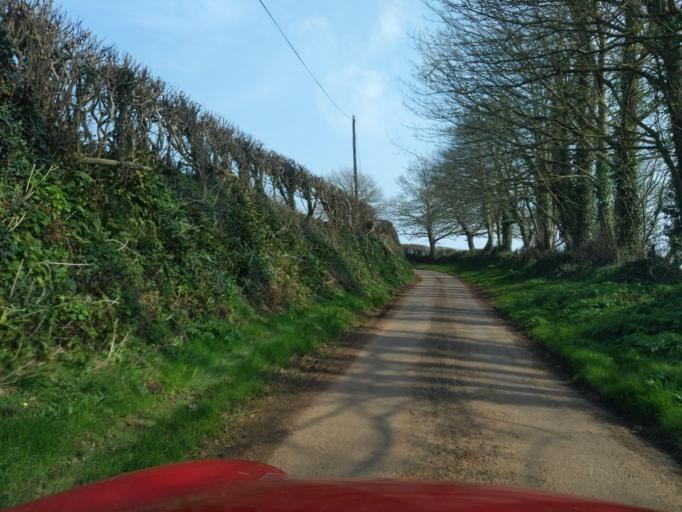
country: GB
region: England
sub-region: Devon
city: Kingsbridge
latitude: 50.2857
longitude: -3.7238
